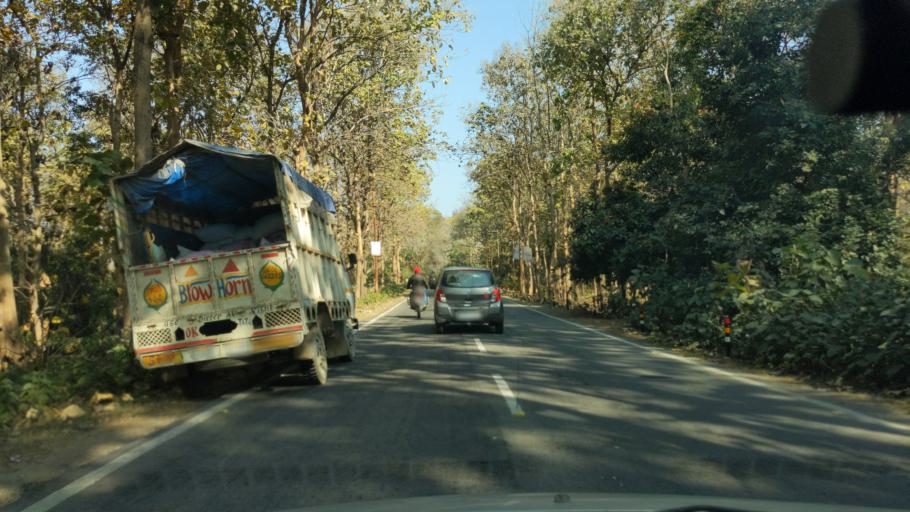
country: IN
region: Uttarakhand
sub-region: Naini Tal
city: Ramnagar
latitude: 29.3838
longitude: 79.1427
